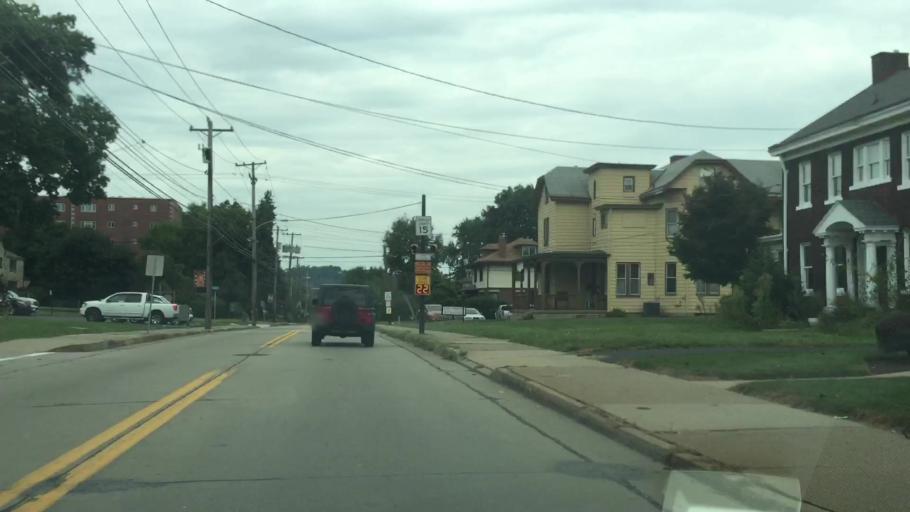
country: US
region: Pennsylvania
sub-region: Allegheny County
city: Carnegie
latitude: 40.4001
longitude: -80.0828
